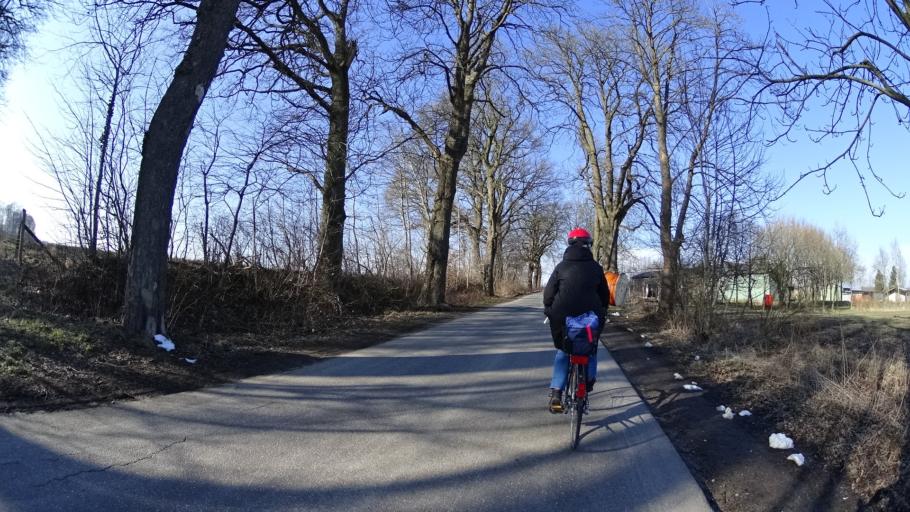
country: DE
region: Schleswig-Holstein
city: Schellhorn
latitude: 54.2522
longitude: 10.3240
